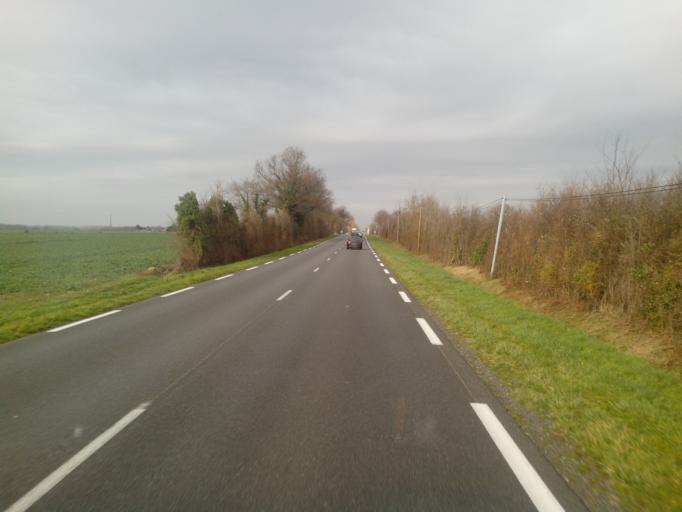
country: FR
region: Poitou-Charentes
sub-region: Departement de la Vienne
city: Saulge
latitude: 46.3086
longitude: 0.8312
